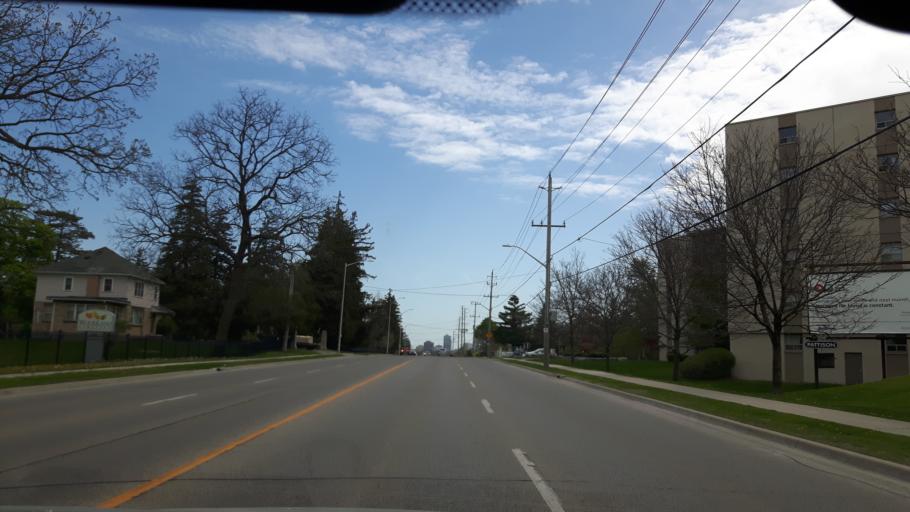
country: CA
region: Ontario
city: London
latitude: 42.9656
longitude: -81.2888
